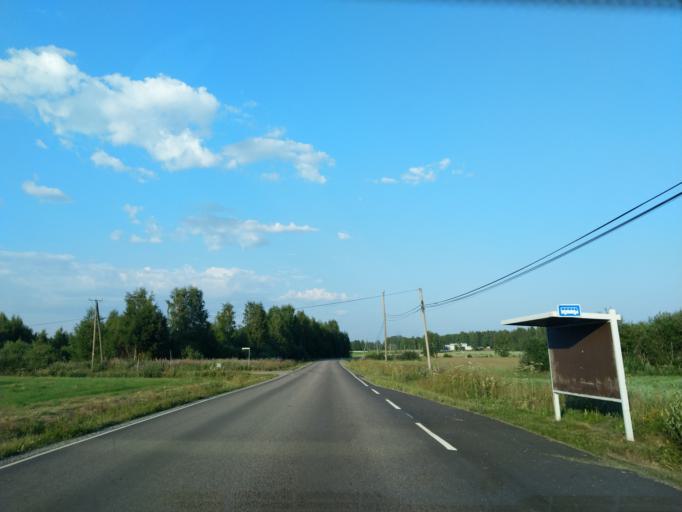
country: FI
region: Satakunta
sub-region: Pohjois-Satakunta
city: Honkajoki
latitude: 61.8202
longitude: 22.2478
